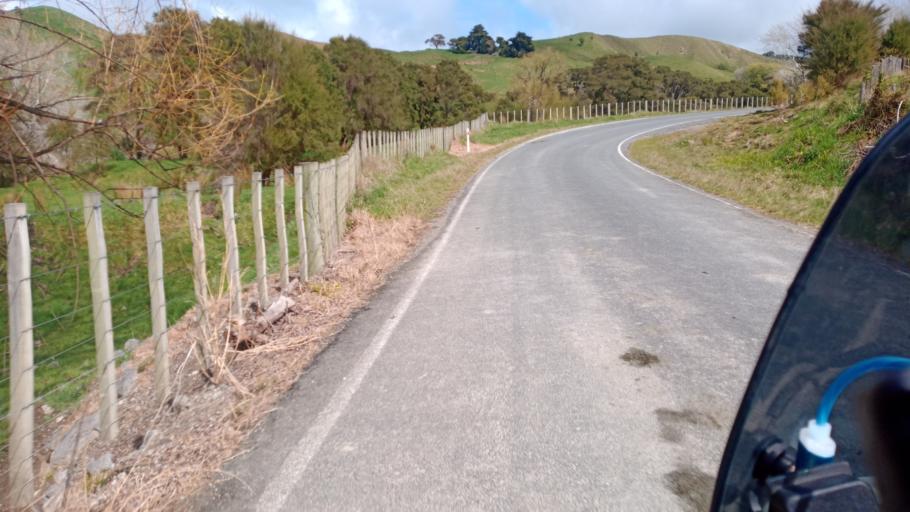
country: NZ
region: Gisborne
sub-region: Gisborne District
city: Gisborne
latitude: -38.5673
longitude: 178.1591
